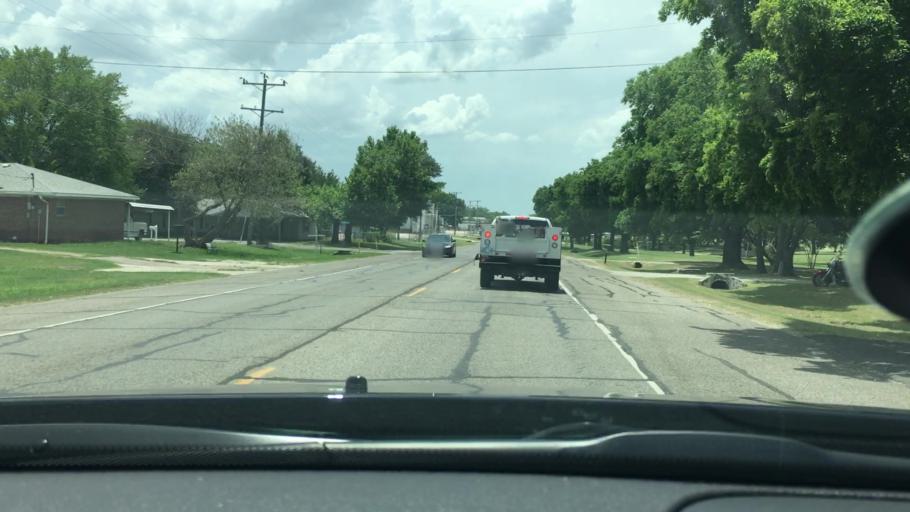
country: US
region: Oklahoma
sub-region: Love County
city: Marietta
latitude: 33.9442
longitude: -97.1263
